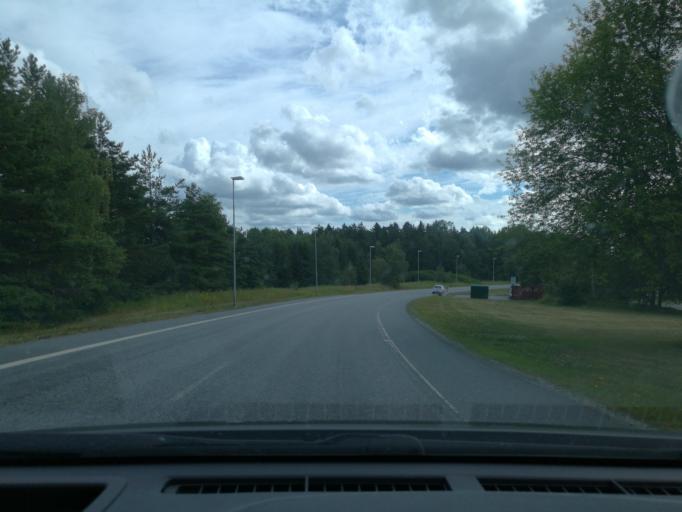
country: SE
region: Stockholm
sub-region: Sigtuna Kommun
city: Marsta
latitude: 59.6397
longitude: 17.8490
